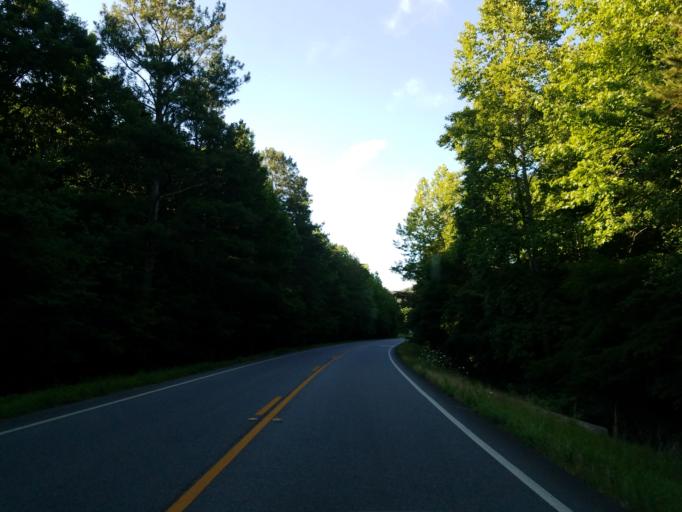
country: US
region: Georgia
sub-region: Whitfield County
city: Dalton
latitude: 34.6523
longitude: -85.0609
